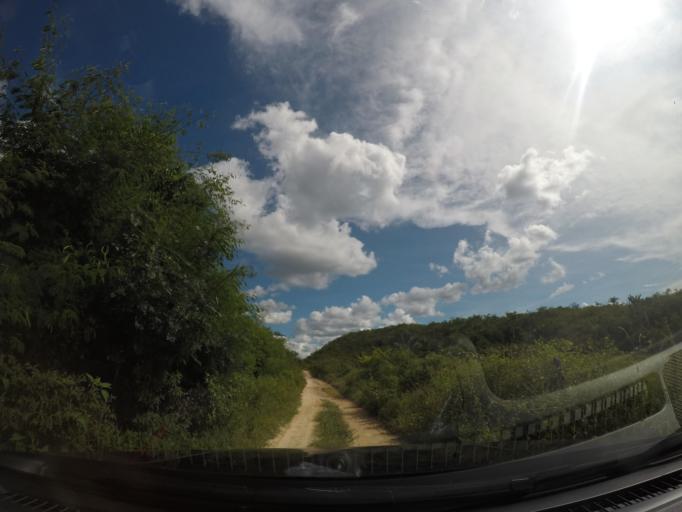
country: BR
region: Bahia
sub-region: Barra Da Estiva
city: Barra da Estiva
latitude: -13.1317
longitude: -41.5950
